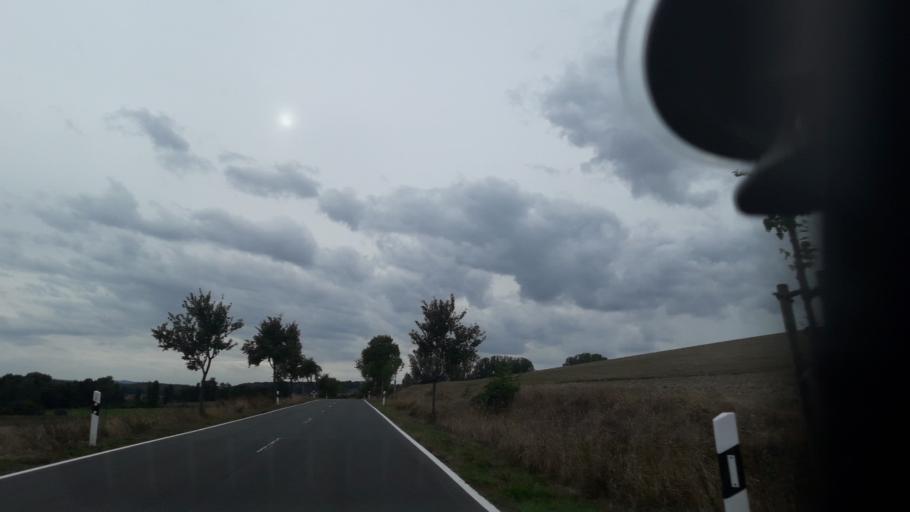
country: DE
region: Lower Saxony
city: Werlaburgdorf
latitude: 52.0499
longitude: 10.5225
